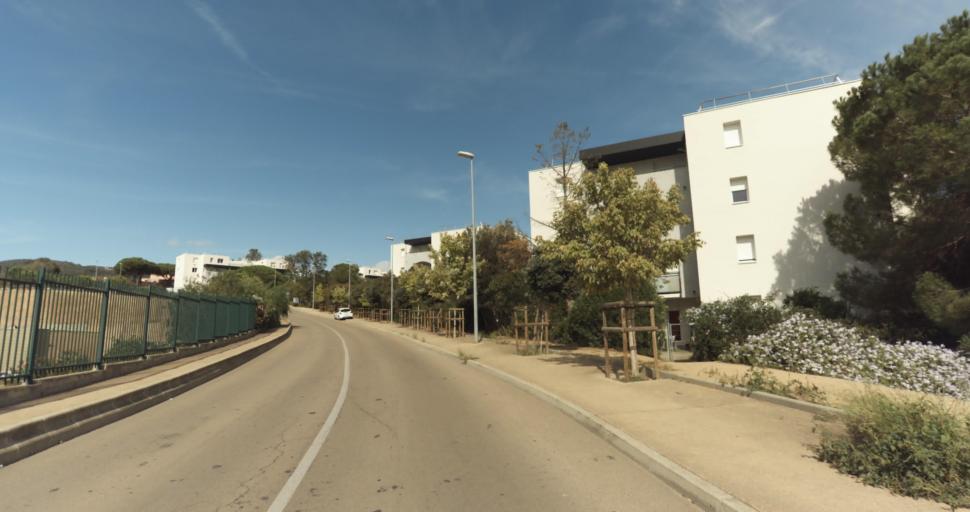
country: FR
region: Corsica
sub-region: Departement de la Corse-du-Sud
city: Ajaccio
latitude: 41.9422
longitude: 8.7469
